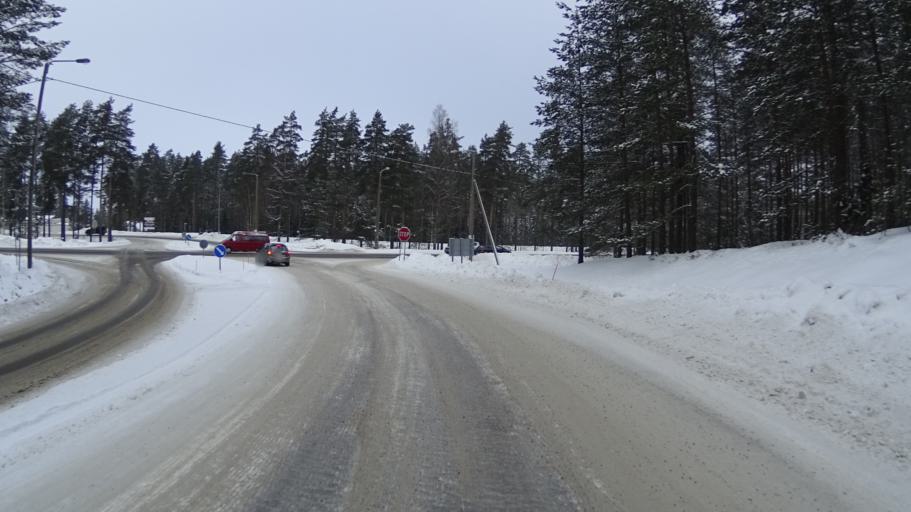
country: FI
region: Uusimaa
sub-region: Helsinki
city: Vihti
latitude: 60.3423
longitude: 24.3076
